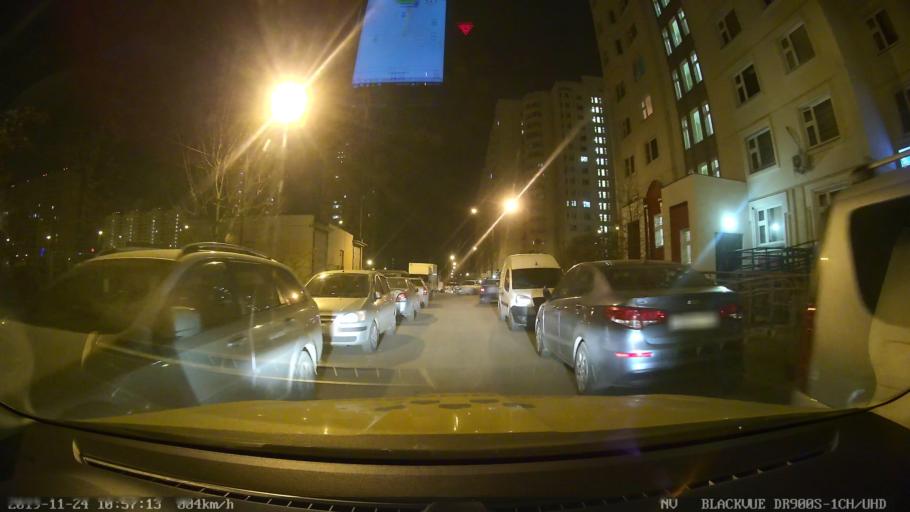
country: RU
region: Moskovskaya
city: Mytishchi
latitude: 55.9092
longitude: 37.7059
